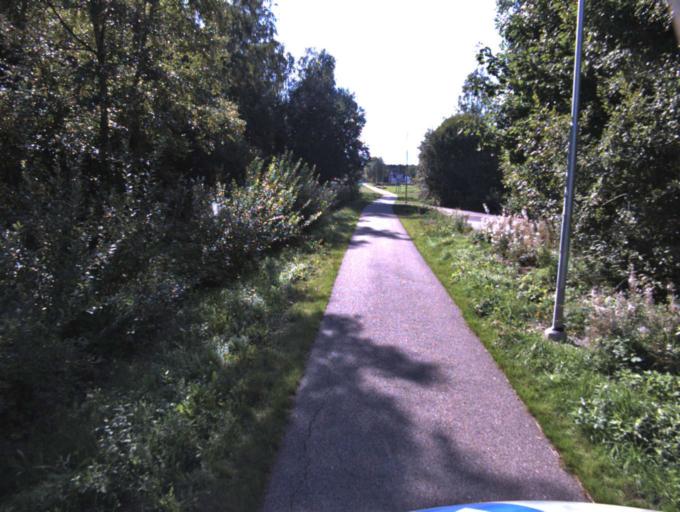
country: SE
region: Vaestra Goetaland
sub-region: Ulricehamns Kommun
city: Ulricehamn
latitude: 57.8424
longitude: 13.2878
